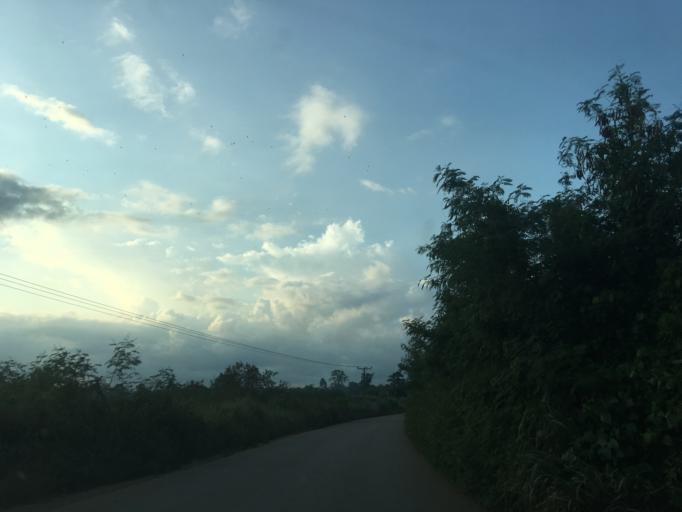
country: GH
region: Western
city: Bibiani
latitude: 6.6368
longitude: -2.4251
